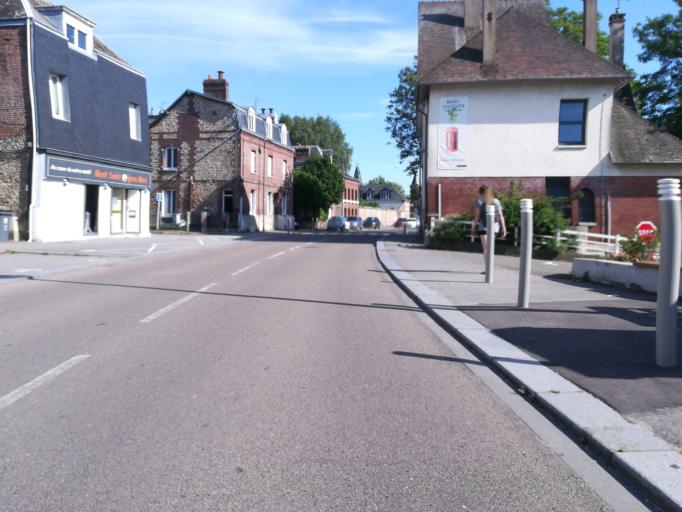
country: FR
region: Haute-Normandie
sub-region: Departement de la Seine-Maritime
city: Mont-Saint-Aignan
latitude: 49.4603
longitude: 1.0799
